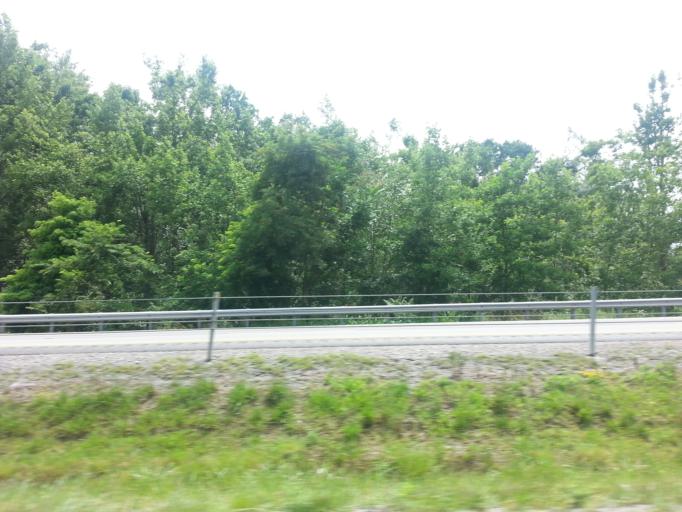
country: US
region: Tennessee
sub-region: Putnam County
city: Monterey
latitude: 36.1125
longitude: -85.2423
